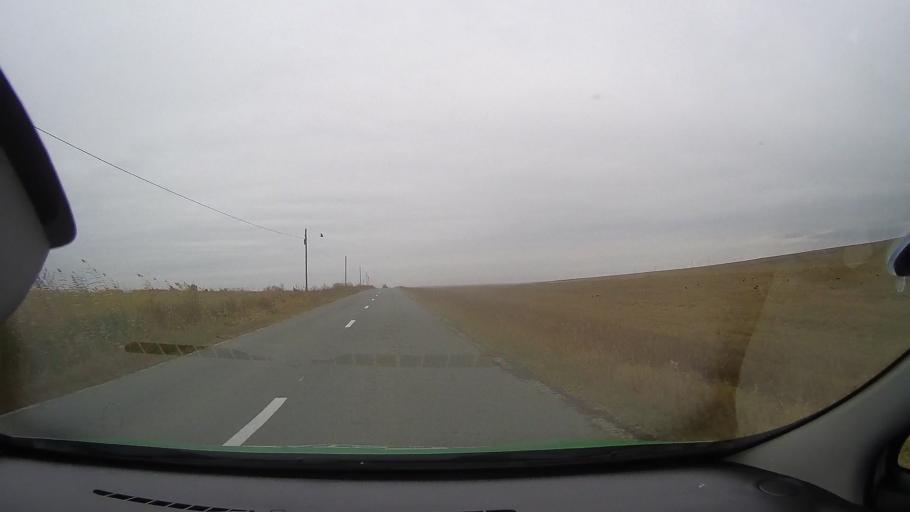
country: RO
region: Constanta
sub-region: Comuna Silistea
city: Silistea
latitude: 44.4377
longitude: 28.2261
